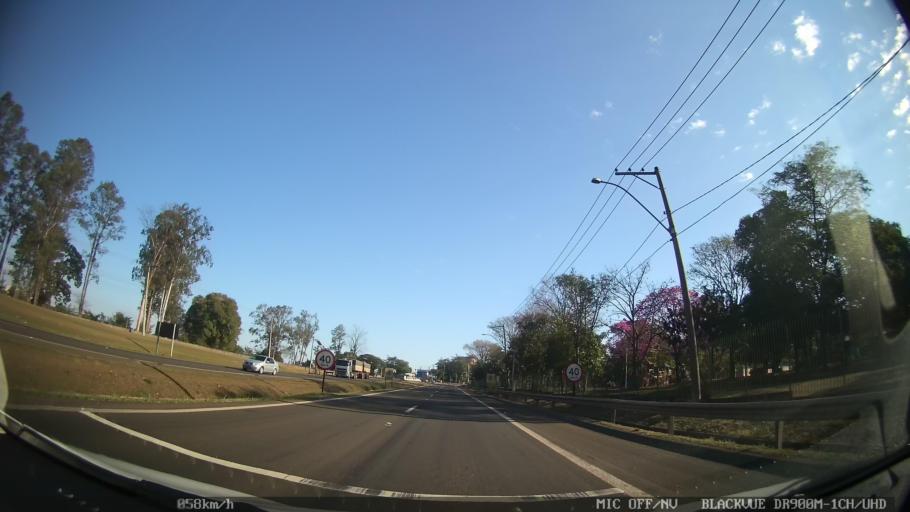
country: BR
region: Sao Paulo
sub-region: Piracicaba
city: Piracicaba
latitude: -22.6969
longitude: -47.6524
